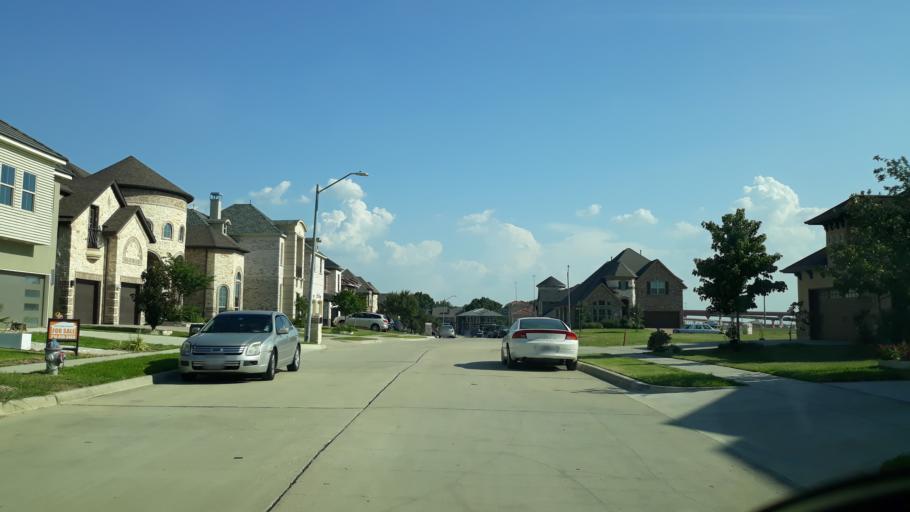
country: US
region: Texas
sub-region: Tarrant County
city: Euless
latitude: 32.8449
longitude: -97.0146
